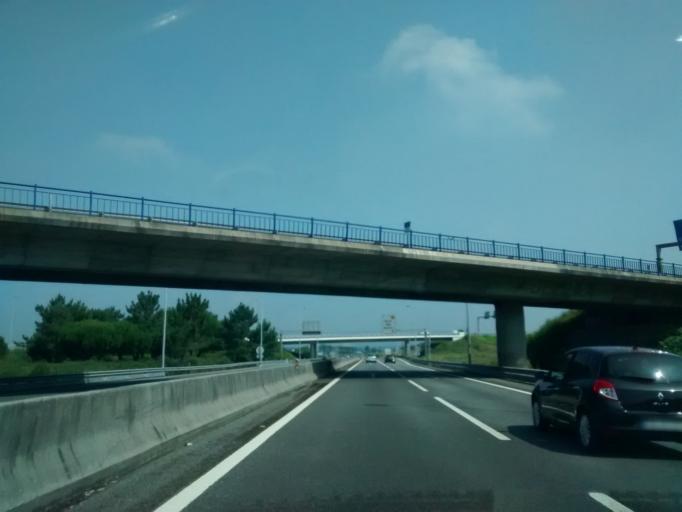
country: PT
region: Braga
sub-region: Esposende
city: Apulia
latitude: 41.4865
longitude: -8.7445
